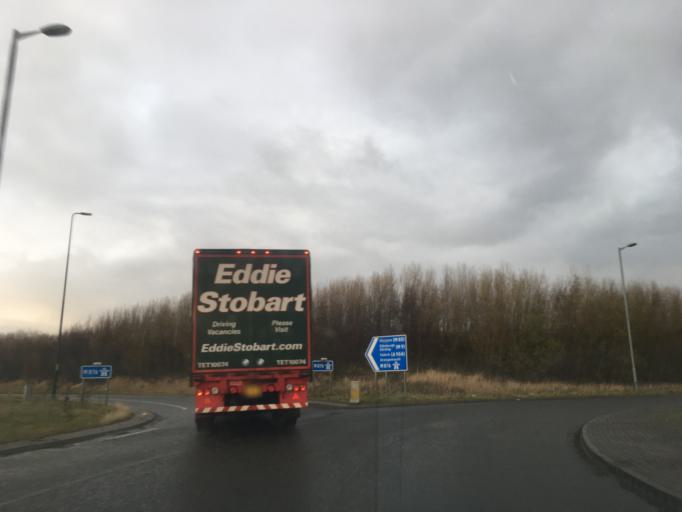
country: GB
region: Scotland
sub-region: Falkirk
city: Airth
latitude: 56.0514
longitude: -3.7597
